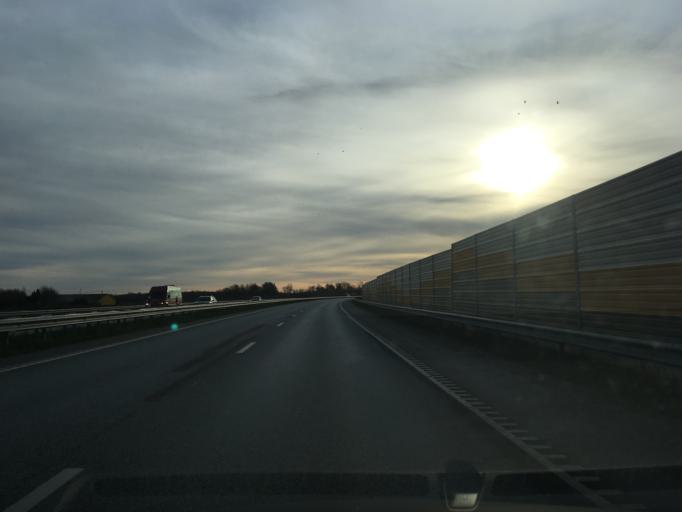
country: EE
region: Ida-Virumaa
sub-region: Johvi vald
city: Johvi
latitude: 59.3793
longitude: 27.3727
